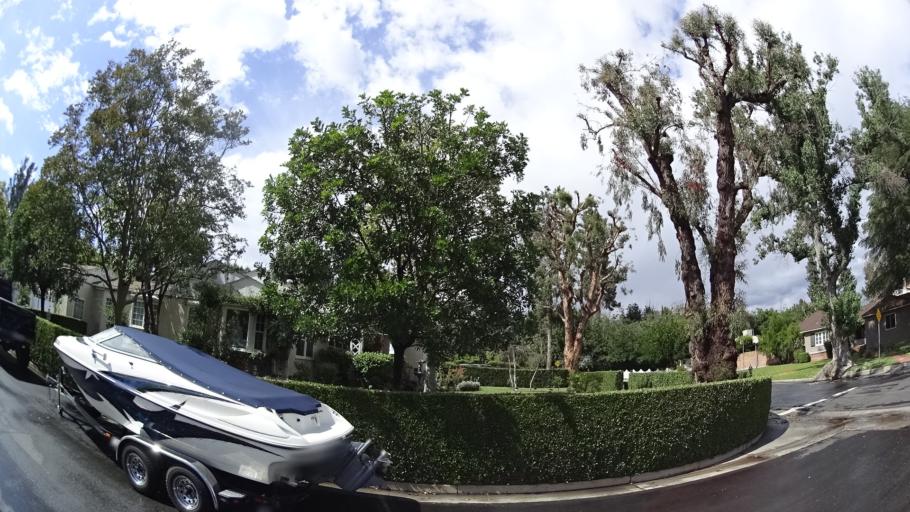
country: US
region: California
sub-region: Los Angeles County
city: Sherman Oaks
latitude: 34.1558
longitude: -118.4162
